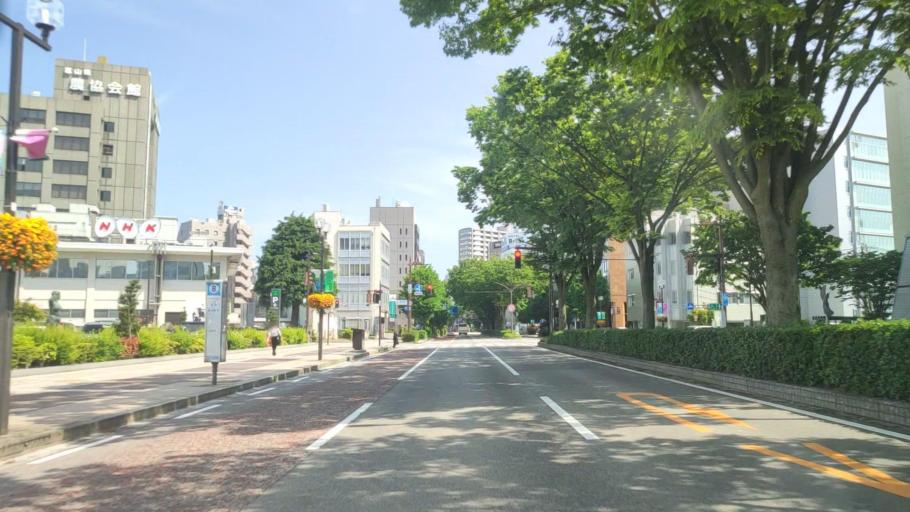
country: JP
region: Toyama
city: Toyama-shi
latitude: 36.6957
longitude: 137.2130
